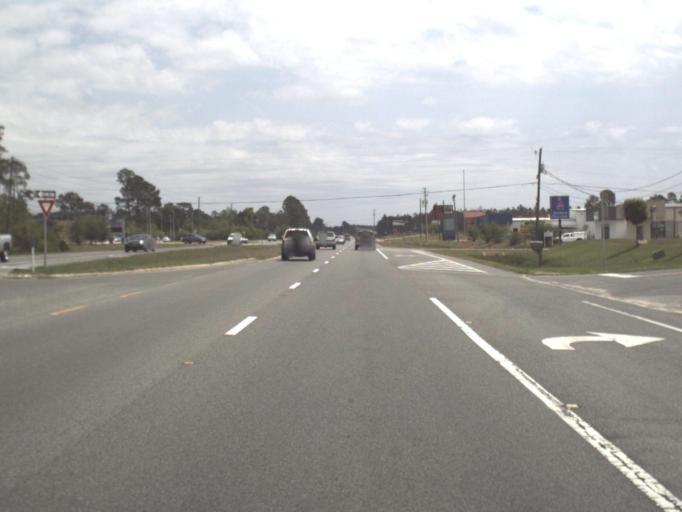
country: US
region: Florida
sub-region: Escambia County
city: Myrtle Grove
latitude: 30.4031
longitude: -87.3385
